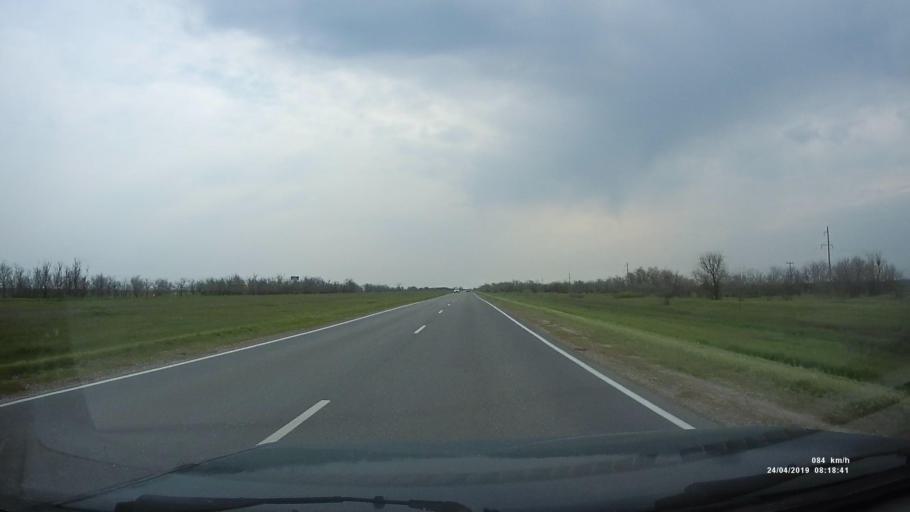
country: RU
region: Kalmykiya
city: Priyutnoye
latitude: 46.1016
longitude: 43.6522
